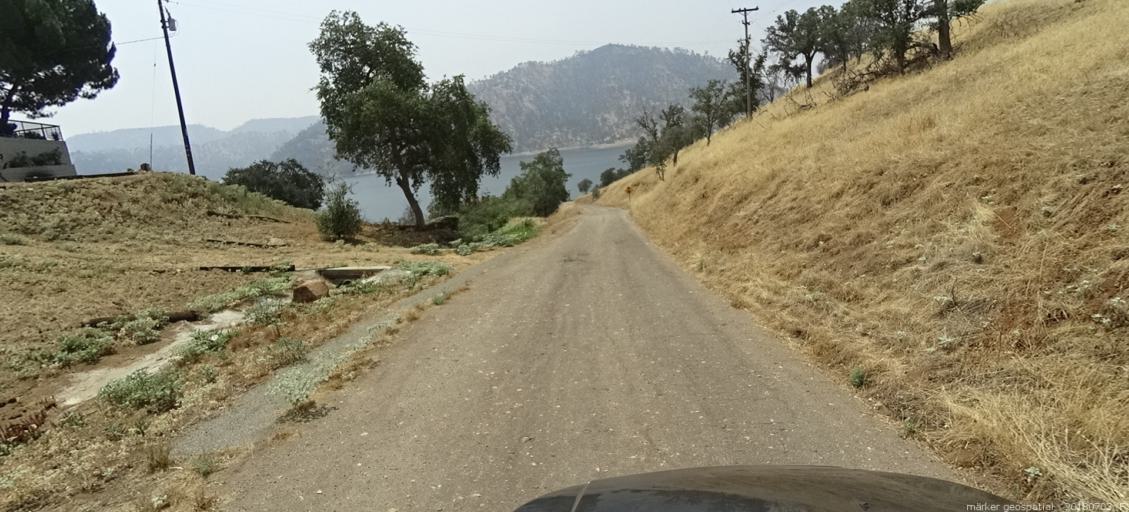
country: US
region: California
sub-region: Fresno County
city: Auberry
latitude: 37.0495
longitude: -119.6496
